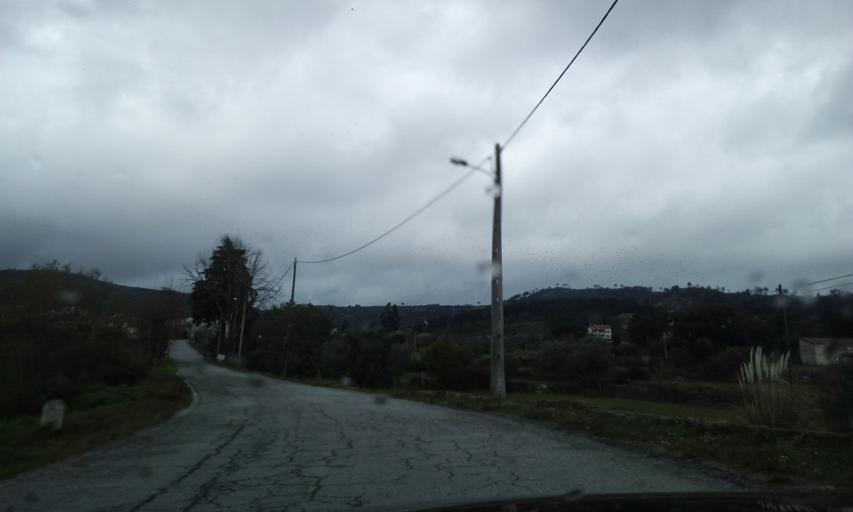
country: PT
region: Guarda
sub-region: Fornos de Algodres
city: Fornos de Algodres
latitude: 40.6144
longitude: -7.5838
